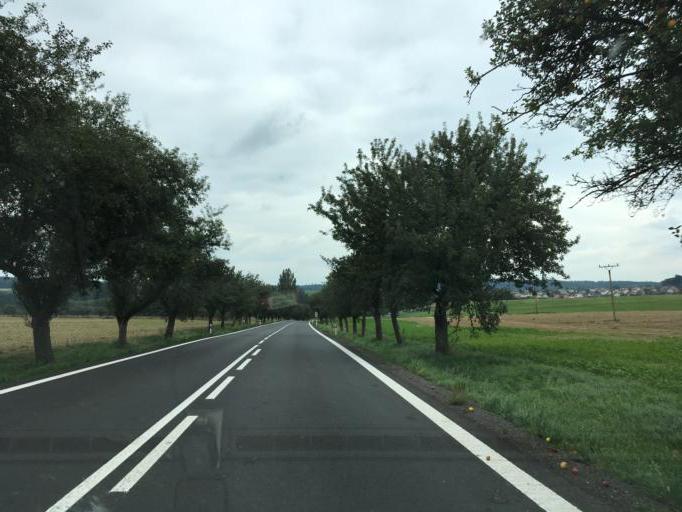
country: CZ
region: Central Bohemia
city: Cechtice
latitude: 49.5708
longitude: 15.1034
